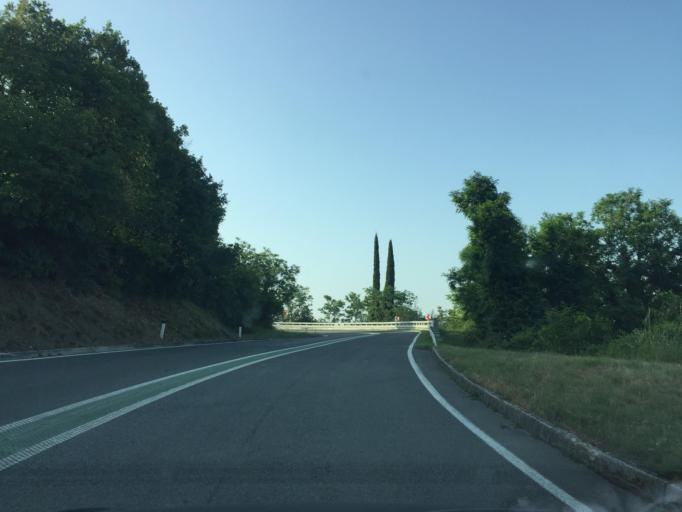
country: SI
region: Koper-Capodistria
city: Sv. Anton
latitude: 45.5486
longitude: 13.8785
